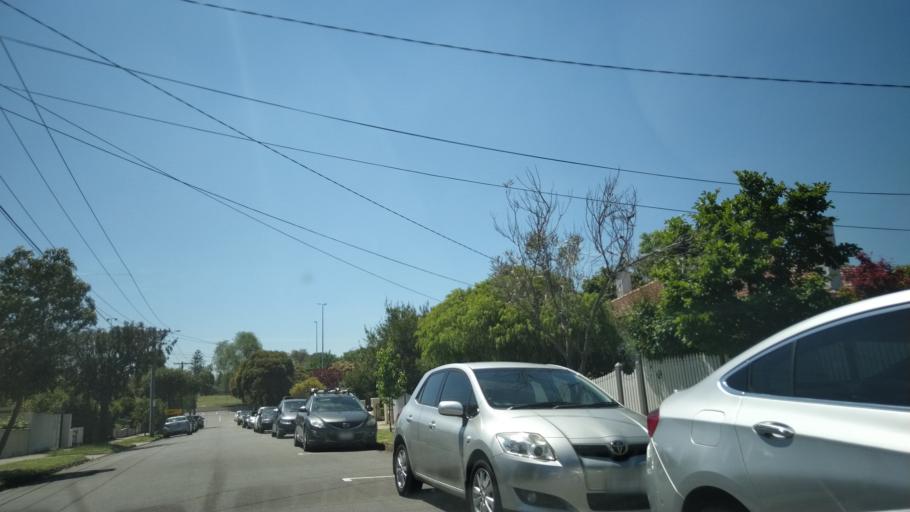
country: AU
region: Victoria
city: Ormond
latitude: -37.9009
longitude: 145.0395
